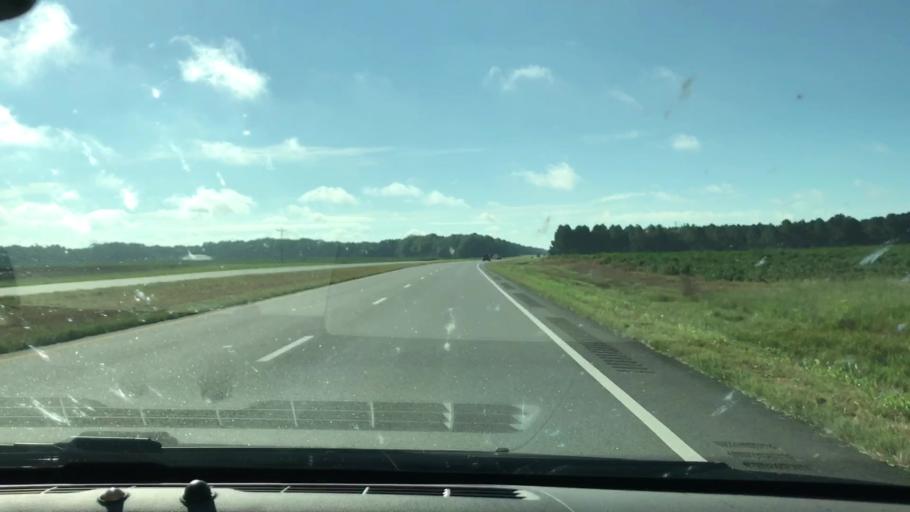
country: US
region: Georgia
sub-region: Terrell County
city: Dawson
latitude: 31.6987
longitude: -84.3223
